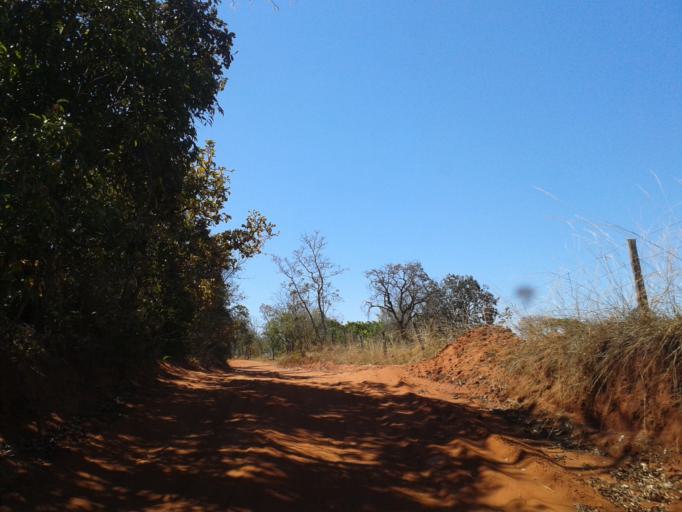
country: BR
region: Minas Gerais
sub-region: Ituiutaba
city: Ituiutaba
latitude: -19.0919
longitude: -49.2971
